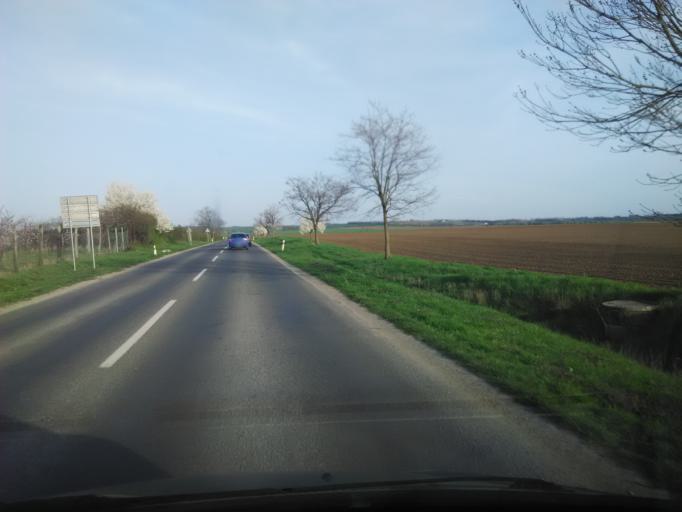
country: SK
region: Nitriansky
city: Surany
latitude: 48.0920
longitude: 18.2622
